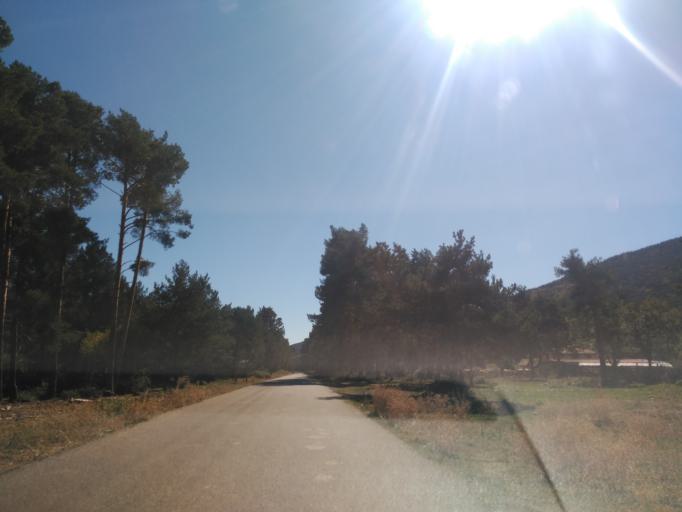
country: ES
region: Castille and Leon
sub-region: Provincia de Soria
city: Vinuesa
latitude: 41.9434
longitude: -2.7801
